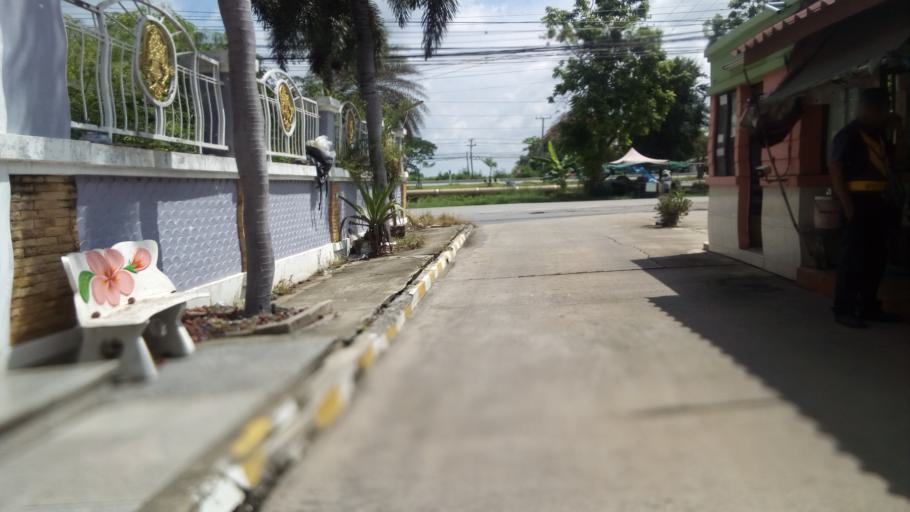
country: TH
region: Pathum Thani
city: Nong Suea
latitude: 14.0643
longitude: 100.8606
